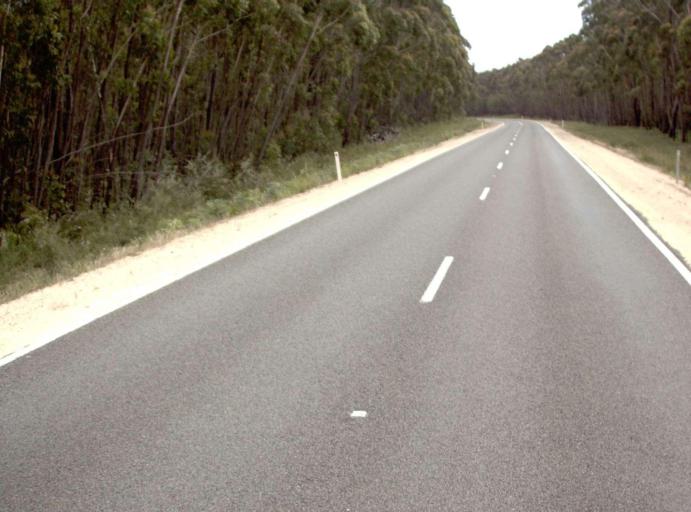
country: AU
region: New South Wales
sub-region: Bega Valley
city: Eden
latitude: -37.5347
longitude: 149.4810
